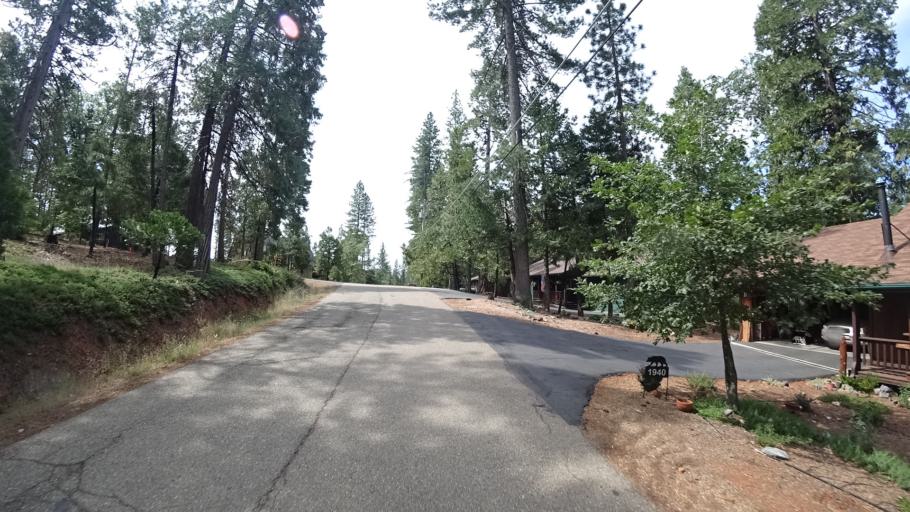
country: US
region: California
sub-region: Calaveras County
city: Arnold
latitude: 38.2411
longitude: -120.3557
